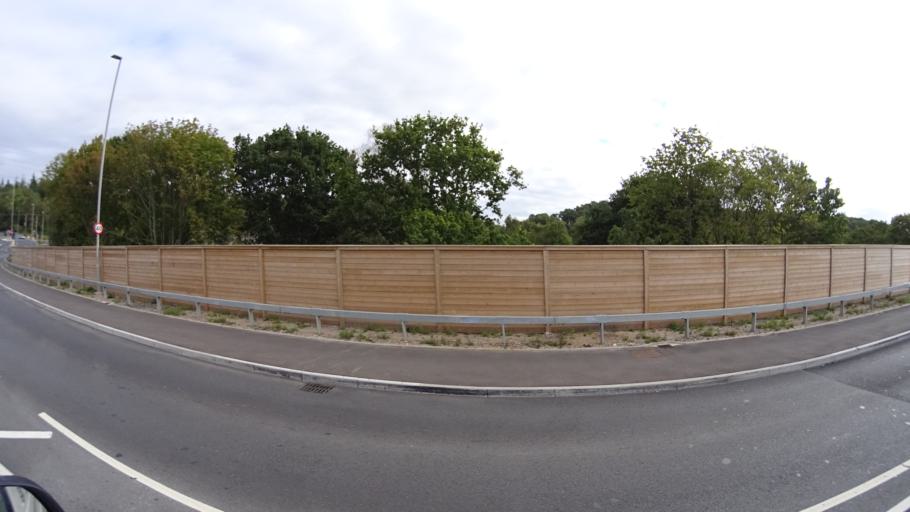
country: GB
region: England
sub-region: Dorset
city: Christchurch
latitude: 50.7633
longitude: -1.8118
